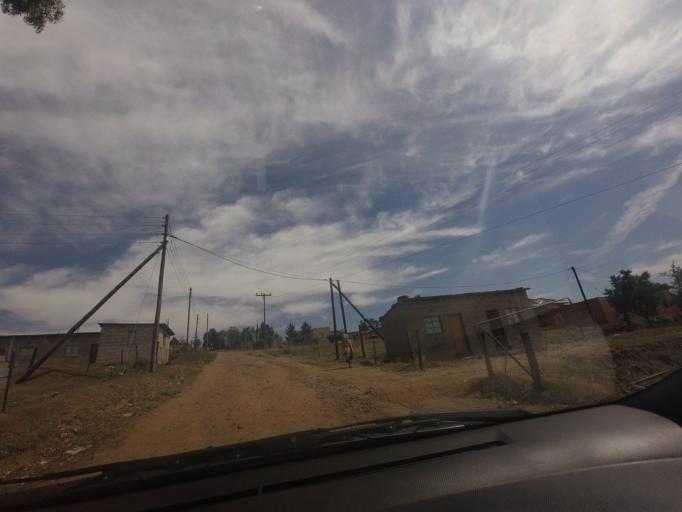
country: LS
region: Berea
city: Teyateyaneng
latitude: -29.1514
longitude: 27.7550
